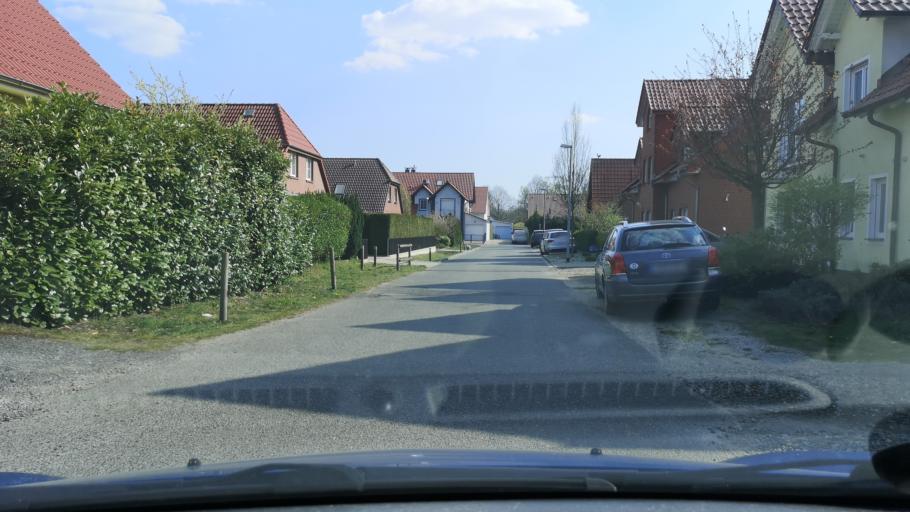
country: DE
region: Lower Saxony
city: Langenhagen
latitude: 52.4440
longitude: 9.6698
